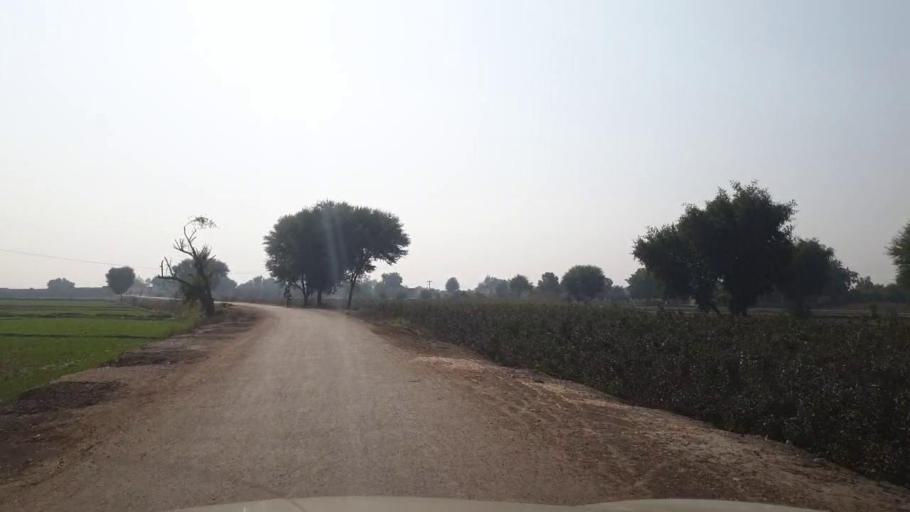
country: PK
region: Sindh
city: Bhan
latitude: 26.5036
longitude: 67.7902
